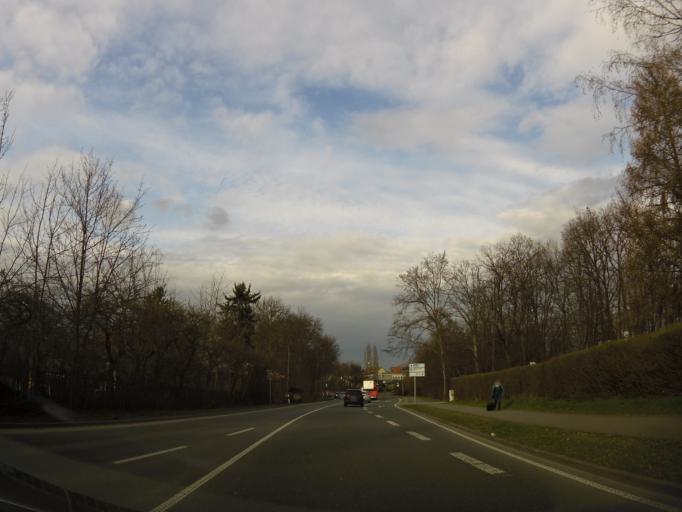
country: DE
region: Thuringia
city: Weimar
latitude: 50.9613
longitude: 11.3174
